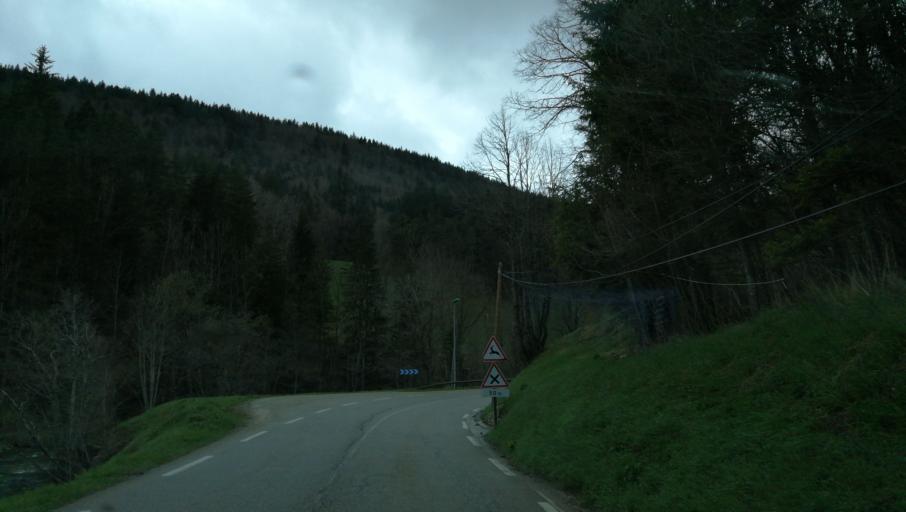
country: FR
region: Rhone-Alpes
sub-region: Departement de l'Isere
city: Villard-de-Lans
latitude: 45.0761
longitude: 5.5378
